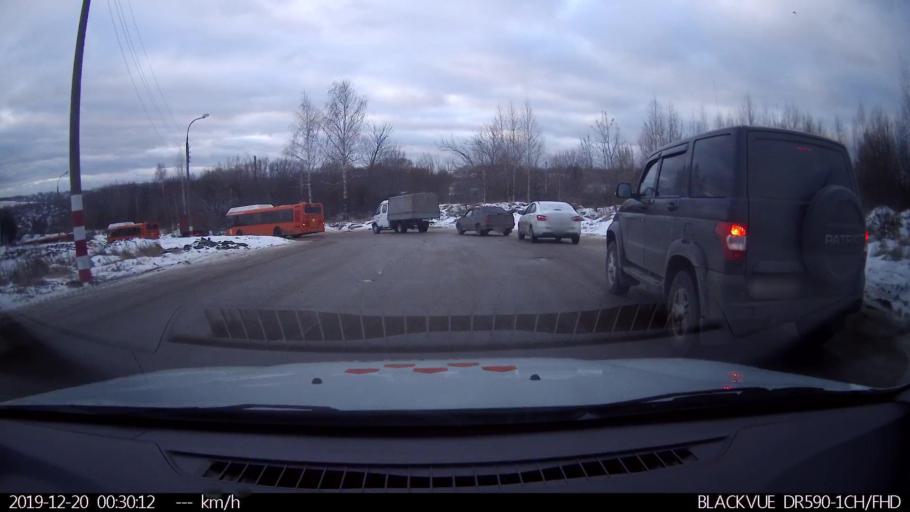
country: RU
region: Vladimir
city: Yur'yev-Pol'skiy
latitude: 56.5290
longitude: 39.6433
